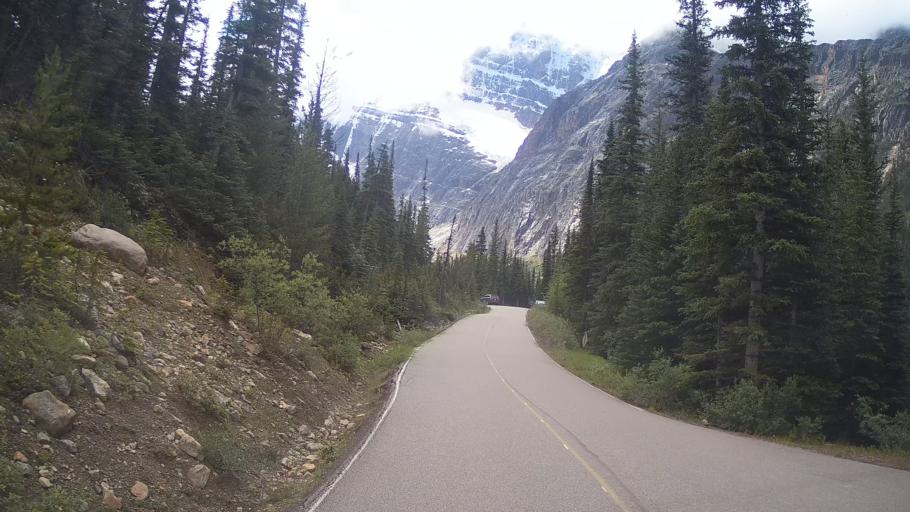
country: CA
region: Alberta
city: Jasper Park Lodge
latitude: 52.7018
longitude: -118.0596
